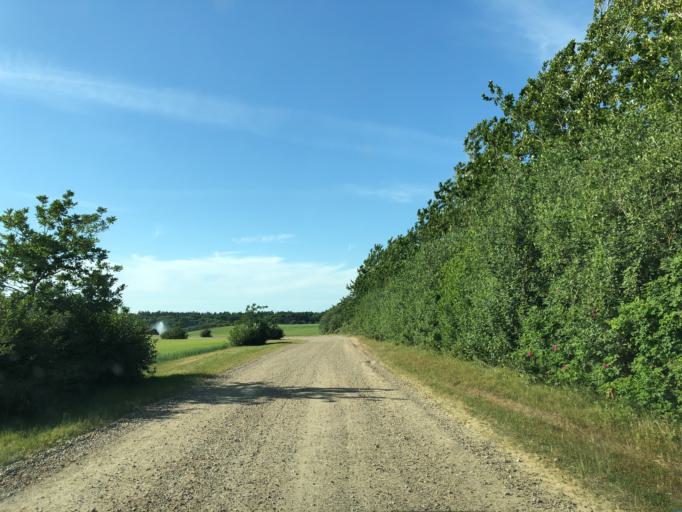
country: DK
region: Central Jutland
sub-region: Holstebro Kommune
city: Ulfborg
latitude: 56.3194
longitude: 8.3973
